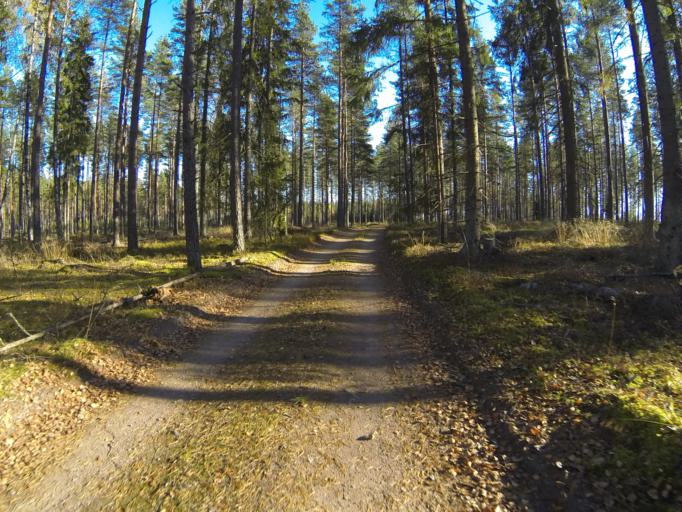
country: FI
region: Varsinais-Suomi
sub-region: Salo
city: Saerkisalo
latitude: 60.2137
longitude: 22.9837
